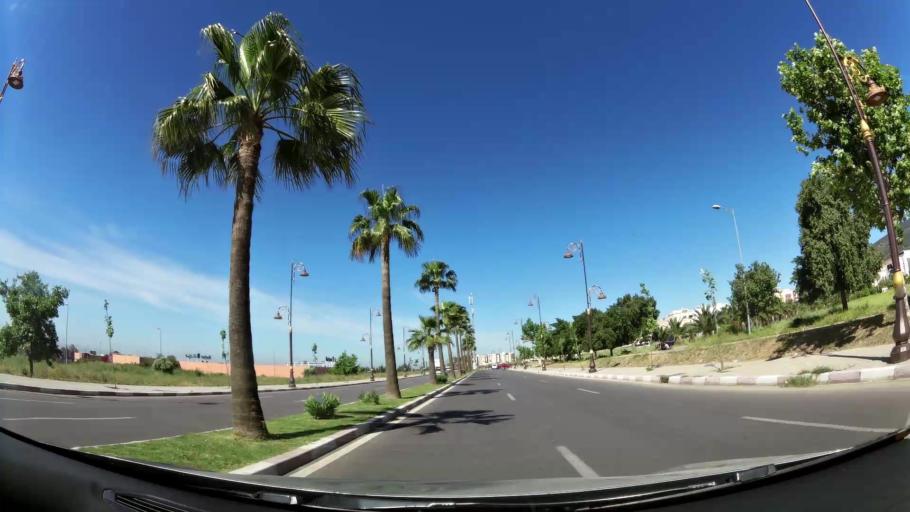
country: MA
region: Fes-Boulemane
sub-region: Fes
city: Fes
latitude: 34.0510
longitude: -5.0334
